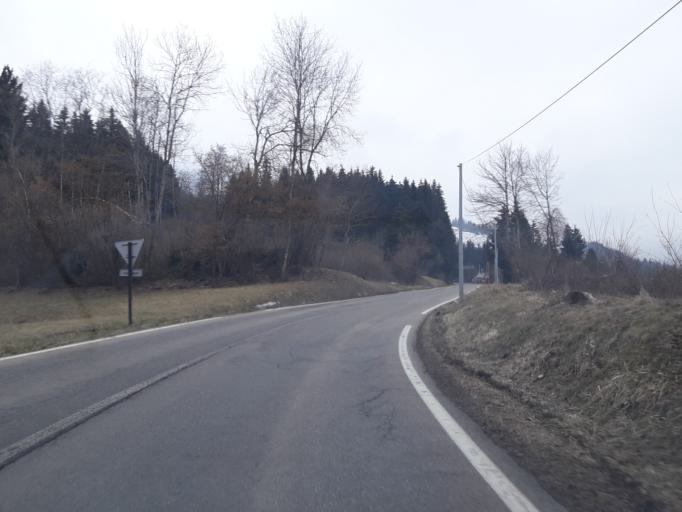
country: FR
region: Rhone-Alpes
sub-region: Departement de l'Isere
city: Theys
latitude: 45.2733
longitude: 5.9884
